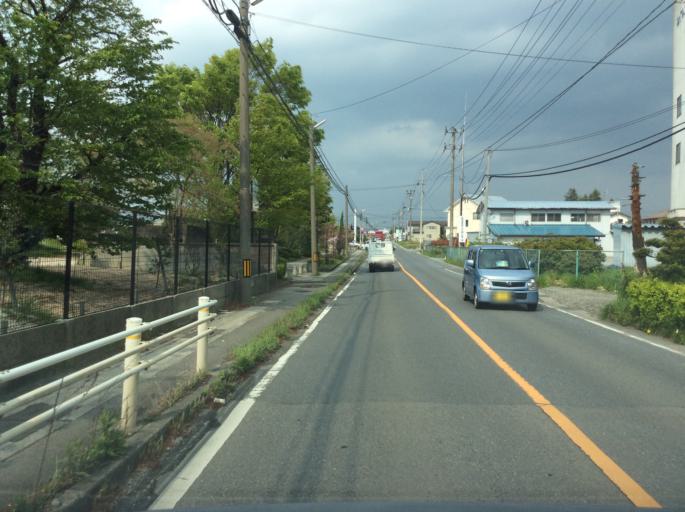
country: JP
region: Fukushima
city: Koriyama
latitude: 37.4171
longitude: 140.4022
